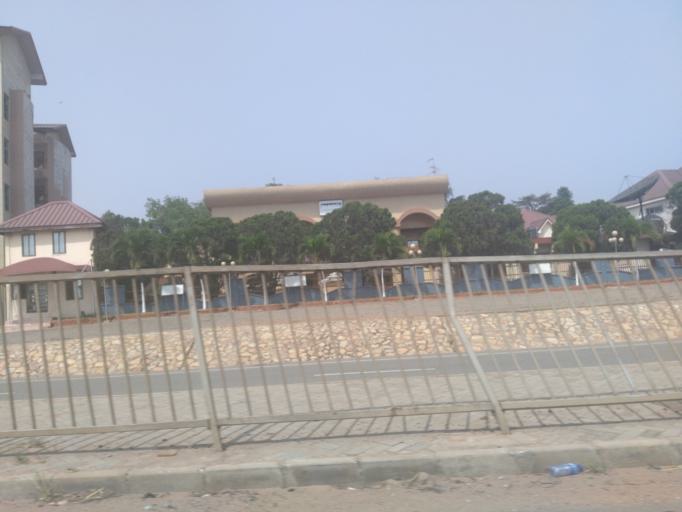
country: GH
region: Greater Accra
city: Dome
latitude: 5.6169
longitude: -0.2008
